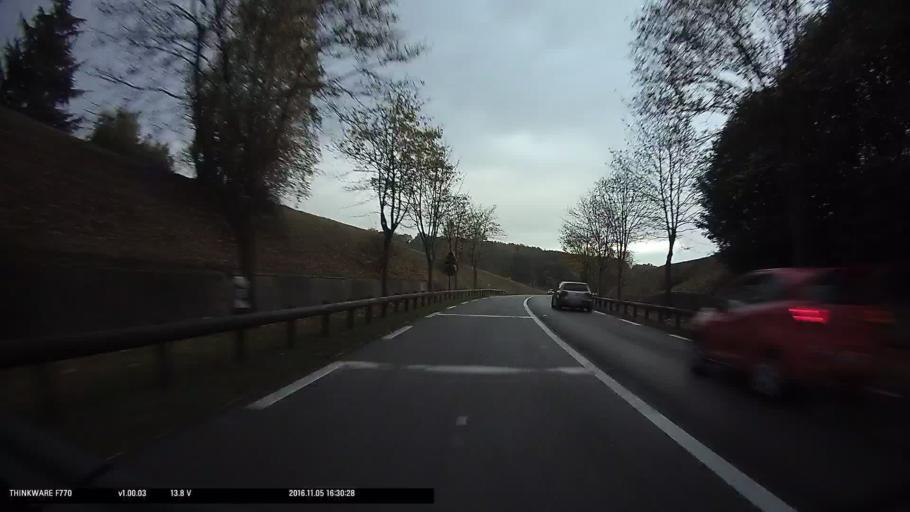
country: FR
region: Ile-de-France
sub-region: Departement du Val-d'Oise
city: Sagy
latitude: 49.0449
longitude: 1.9546
